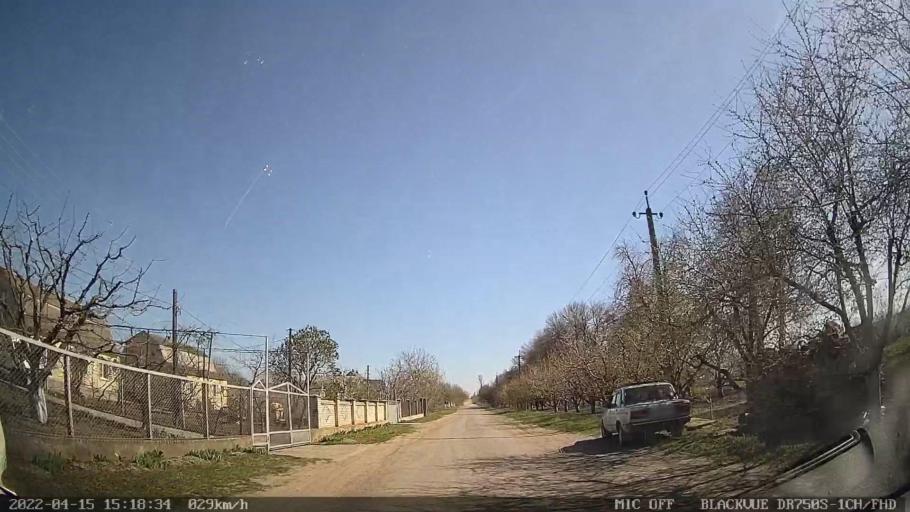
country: MD
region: Raionul Ocnita
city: Otaci
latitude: 48.3901
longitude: 27.9030
